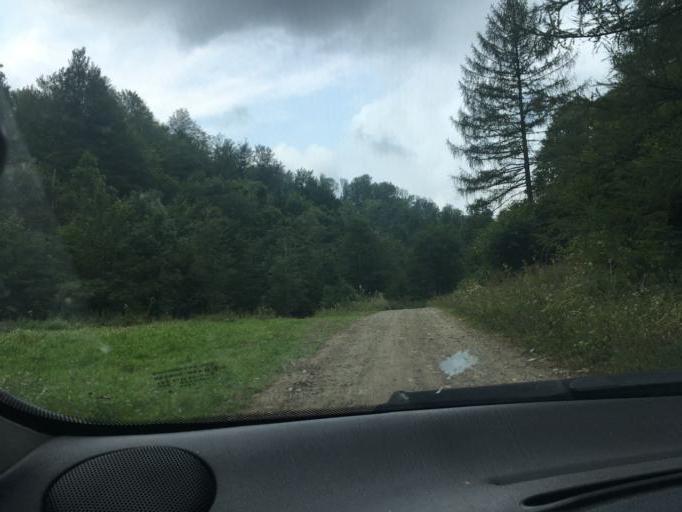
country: PL
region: Subcarpathian Voivodeship
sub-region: Powiat bieszczadzki
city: Lutowiska
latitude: 49.1778
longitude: 22.6187
